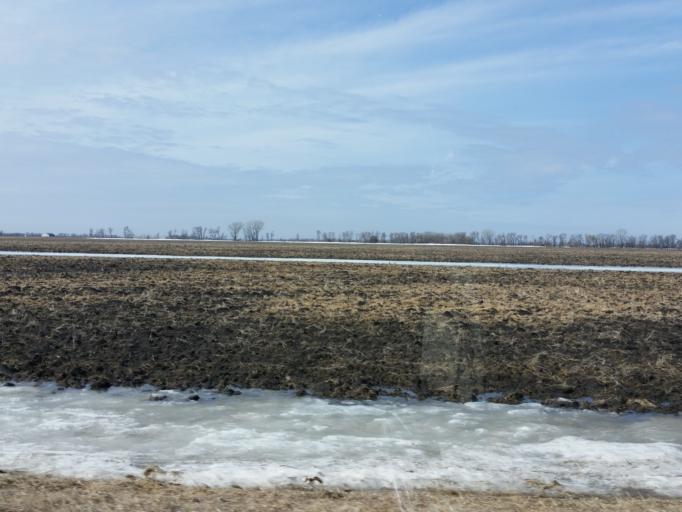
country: US
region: North Dakota
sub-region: Walsh County
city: Grafton
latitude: 48.3425
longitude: -97.2111
